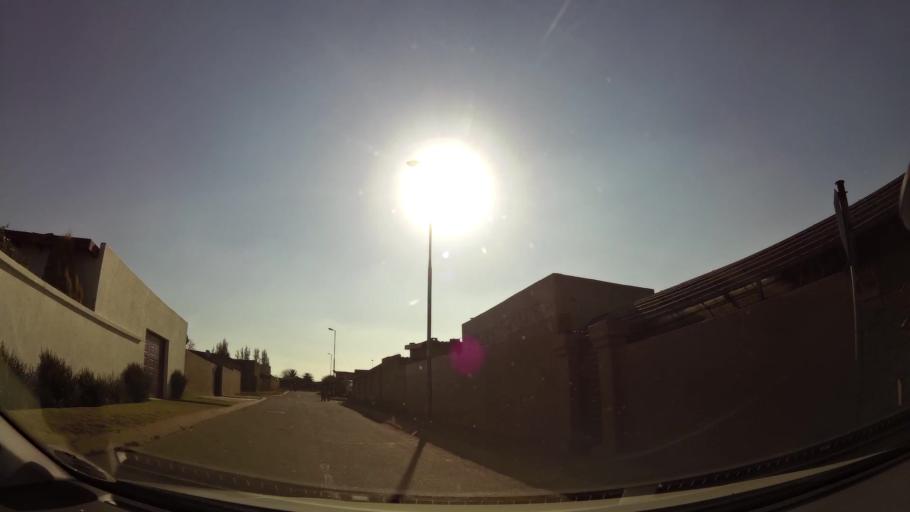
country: ZA
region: Gauteng
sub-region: City of Johannesburg Metropolitan Municipality
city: Soweto
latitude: -26.2769
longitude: 27.8805
